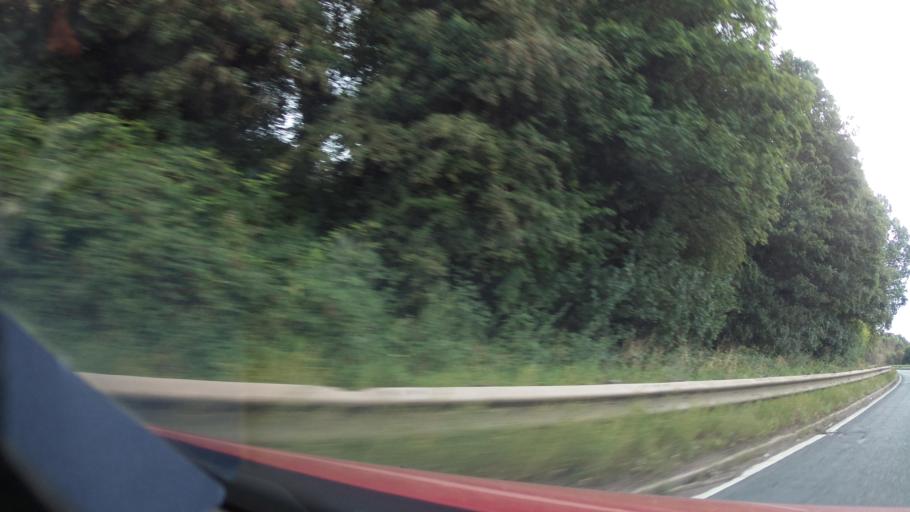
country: GB
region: England
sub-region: Warwickshire
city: Water Orton
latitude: 52.5008
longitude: -1.7128
